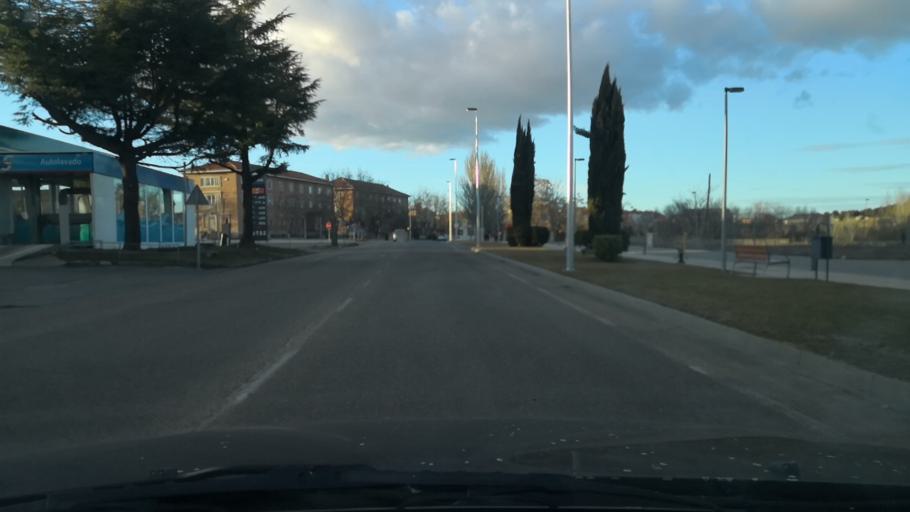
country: ES
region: Castille and Leon
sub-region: Provincia de Valladolid
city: Medina del Campo
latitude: 41.3017
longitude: -4.9086
